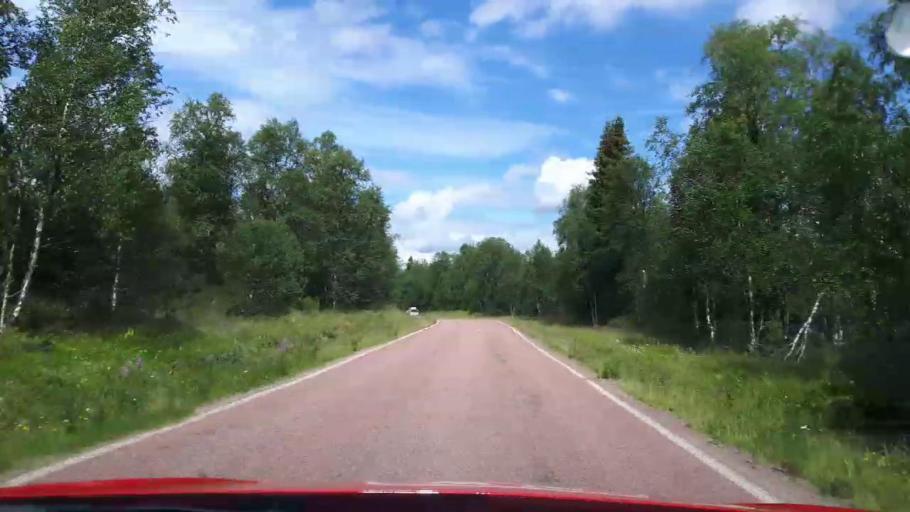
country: NO
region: Hedmark
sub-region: Trysil
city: Innbygda
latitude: 62.0106
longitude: 12.9759
